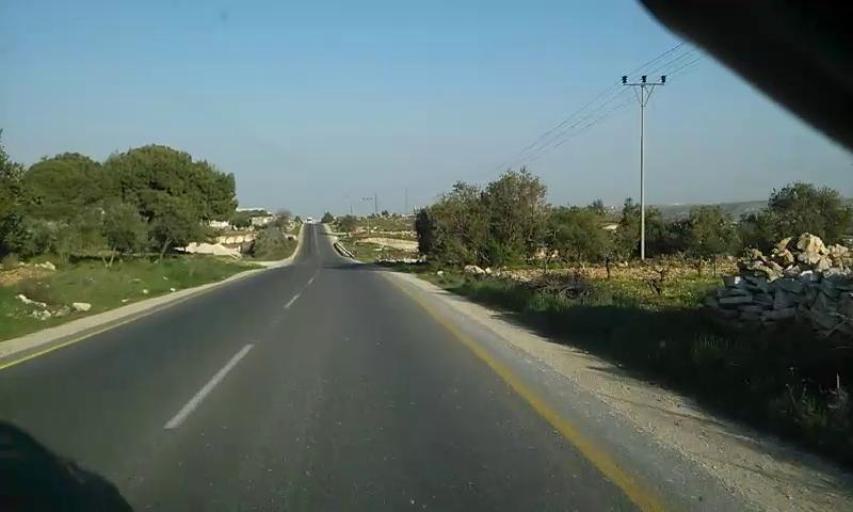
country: PS
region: West Bank
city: Jurat ash Sham`ah
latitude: 31.6480
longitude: 35.1722
